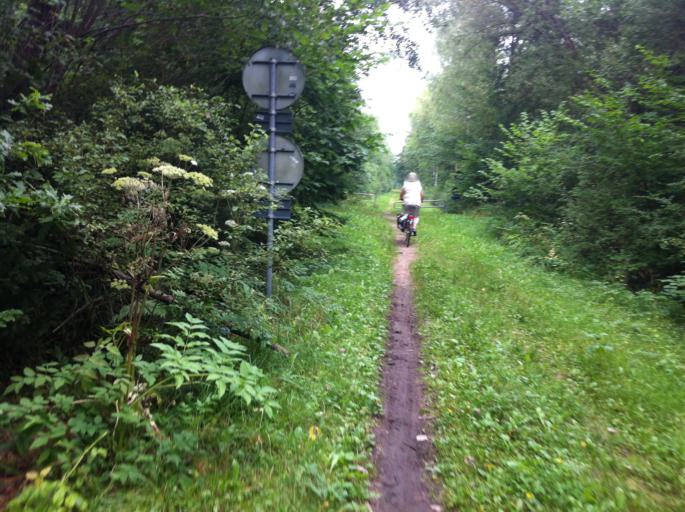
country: SE
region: Skane
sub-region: Horby Kommun
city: Hoerby
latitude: 55.8793
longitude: 13.7492
